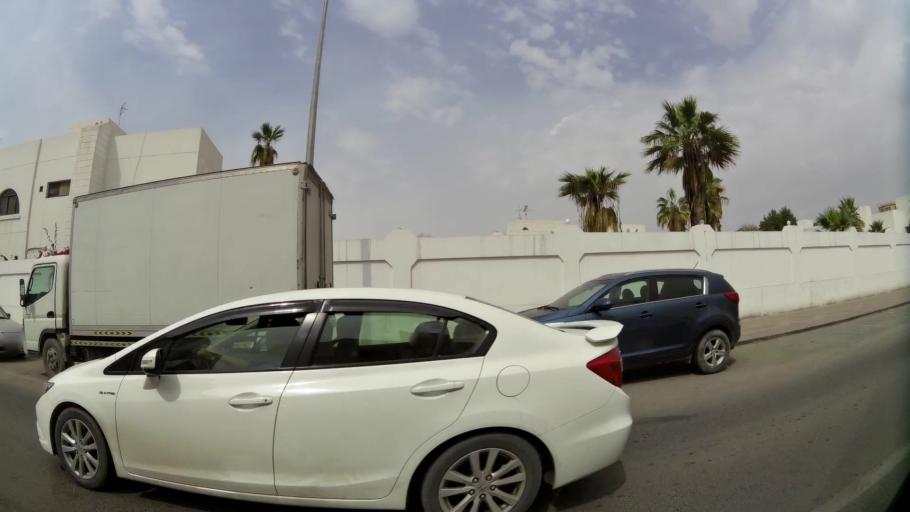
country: QA
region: Baladiyat ad Dawhah
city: Doha
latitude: 25.2829
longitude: 51.5011
